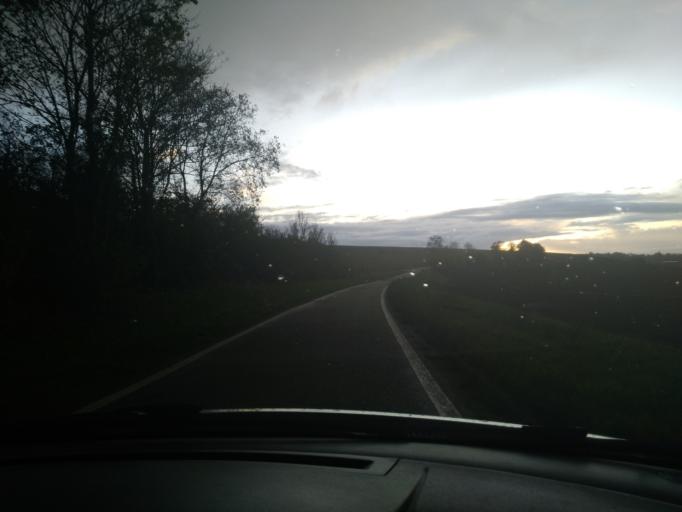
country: FR
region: Ile-de-France
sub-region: Departement des Yvelines
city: Feucherolles
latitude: 48.8516
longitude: 1.9626
